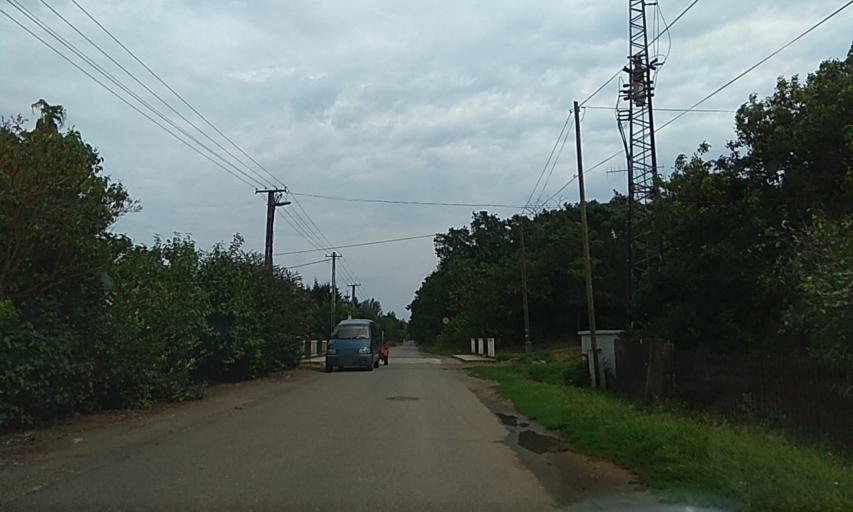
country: HU
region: Szabolcs-Szatmar-Bereg
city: Kotaj
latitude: 48.0034
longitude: 21.7112
